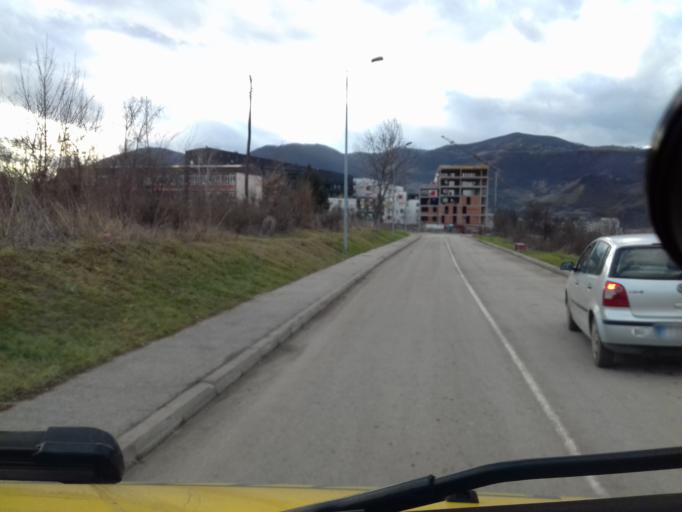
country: BA
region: Federation of Bosnia and Herzegovina
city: Zenica
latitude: 44.2041
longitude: 17.9178
